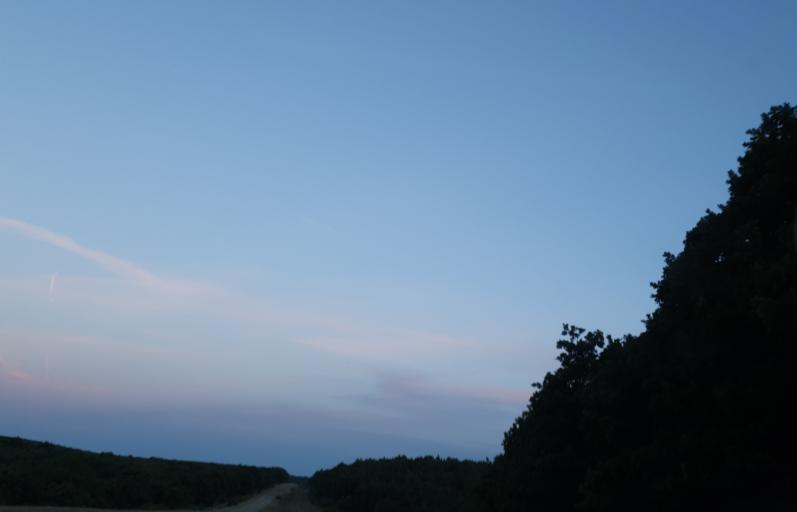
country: TR
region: Kirklareli
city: Salmydessus
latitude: 41.6770
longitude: 28.0898
